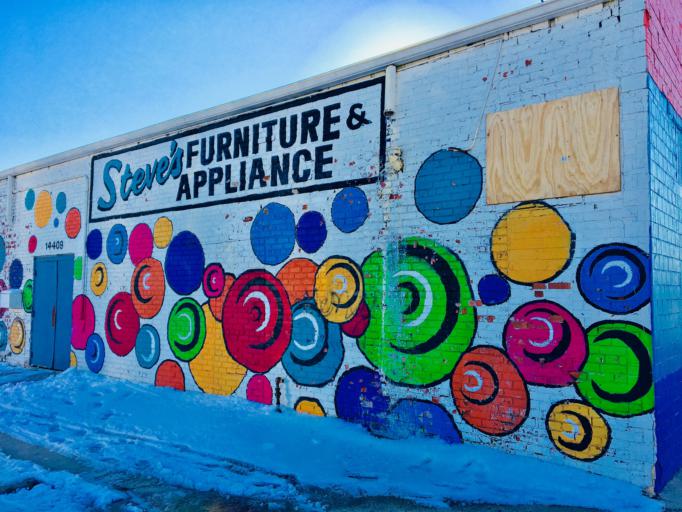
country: US
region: Michigan
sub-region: Wayne County
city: Grosse Pointe Park
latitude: 42.3959
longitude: -82.9590
